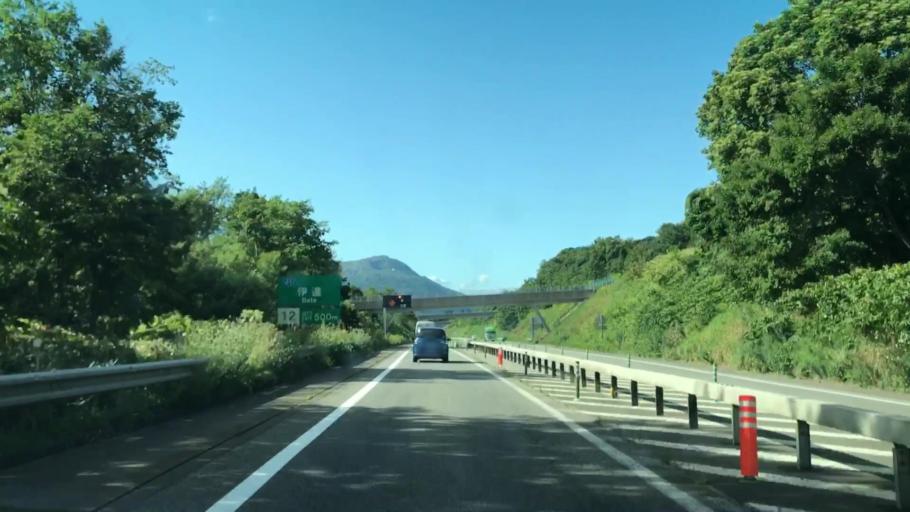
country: JP
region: Hokkaido
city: Date
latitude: 42.4754
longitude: 140.9027
